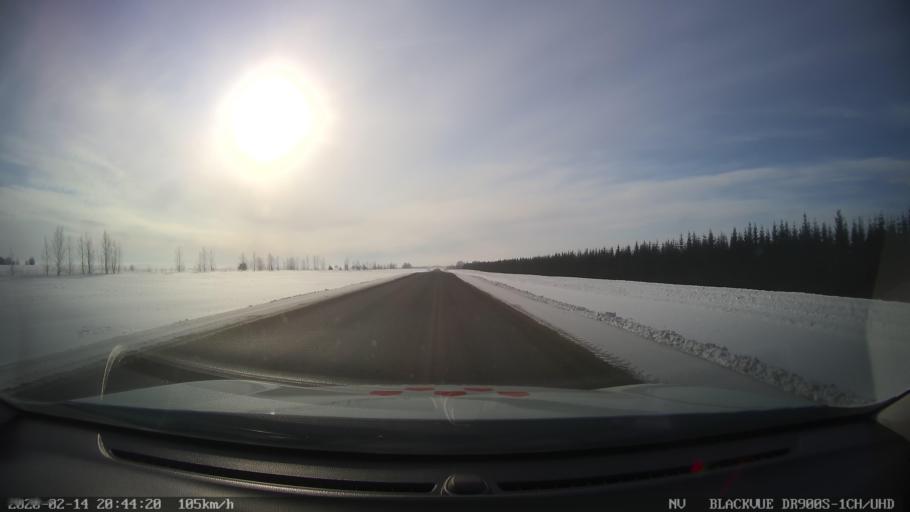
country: RU
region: Tatarstan
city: Kuybyshevskiy Zaton
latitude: 55.2954
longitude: 49.1465
